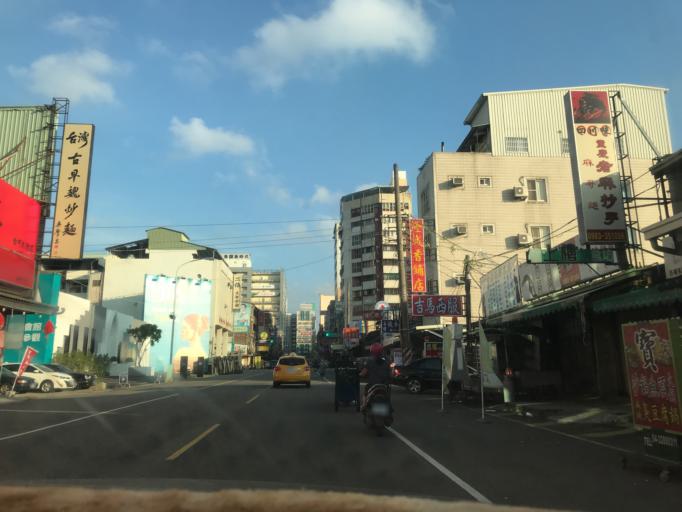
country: TW
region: Taiwan
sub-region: Taichung City
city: Taichung
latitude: 24.1331
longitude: 120.6896
